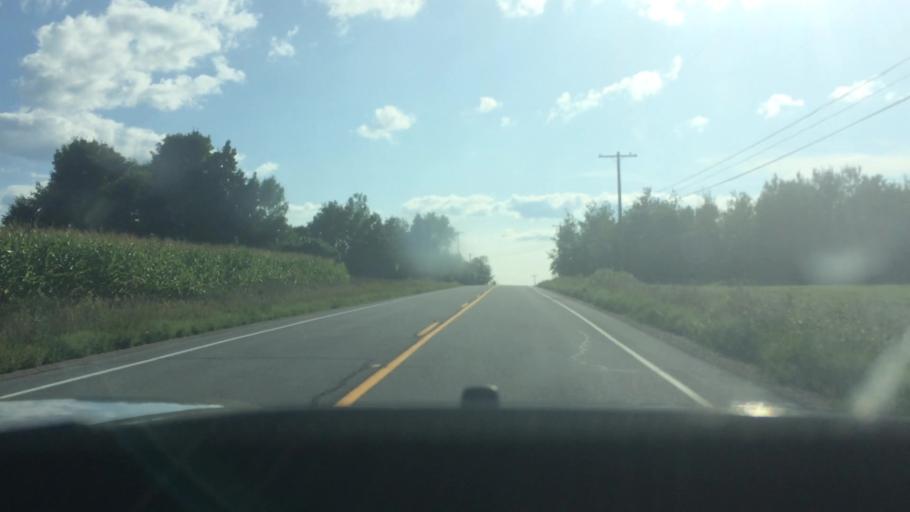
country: CA
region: Ontario
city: Cornwall
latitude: 44.7372
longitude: -74.5904
